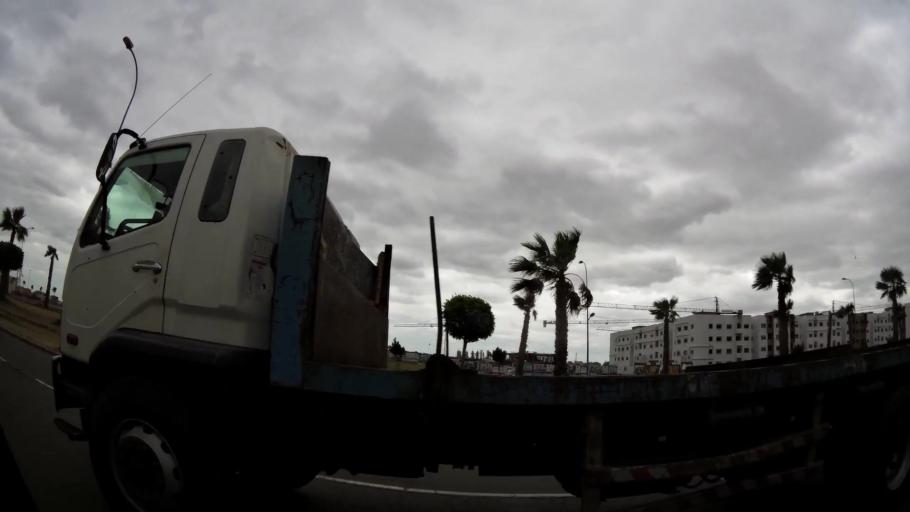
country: MA
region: Grand Casablanca
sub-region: Mediouna
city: Tit Mellil
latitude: 33.5540
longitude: -7.5480
